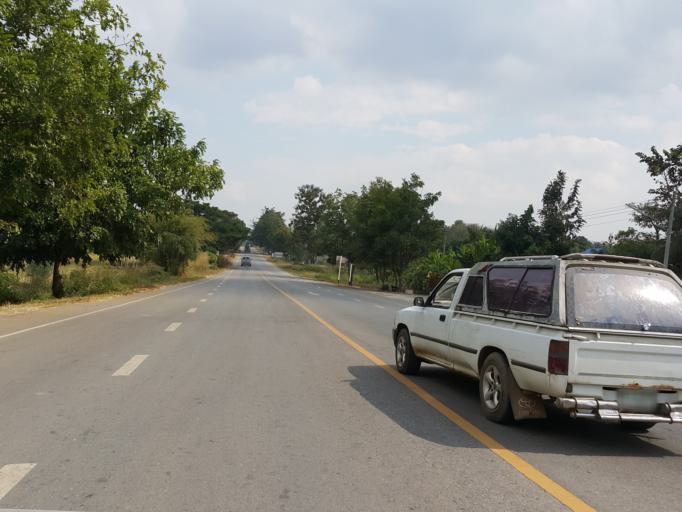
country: TH
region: Sukhothai
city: Thung Saliam
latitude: 17.3324
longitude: 99.5383
